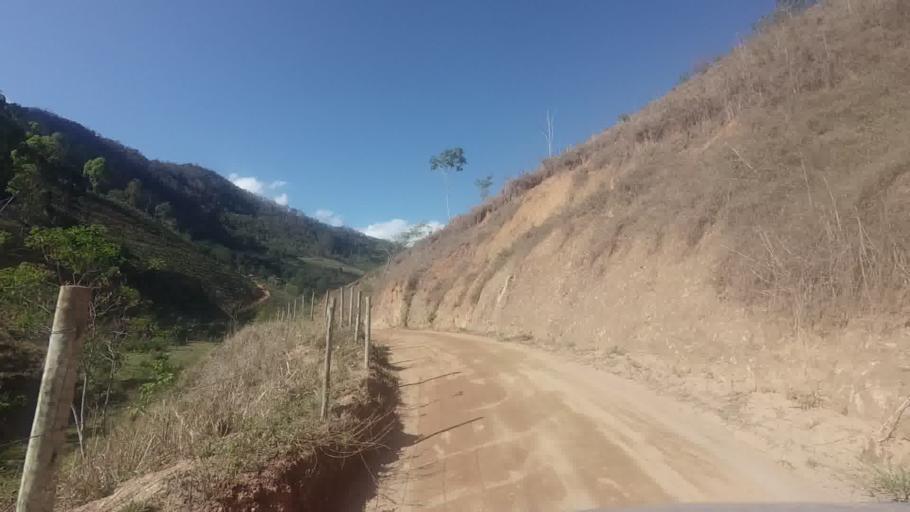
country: BR
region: Espirito Santo
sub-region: Sao Jose Do Calcado
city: Sao Jose do Calcado
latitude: -21.0351
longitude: -41.5987
